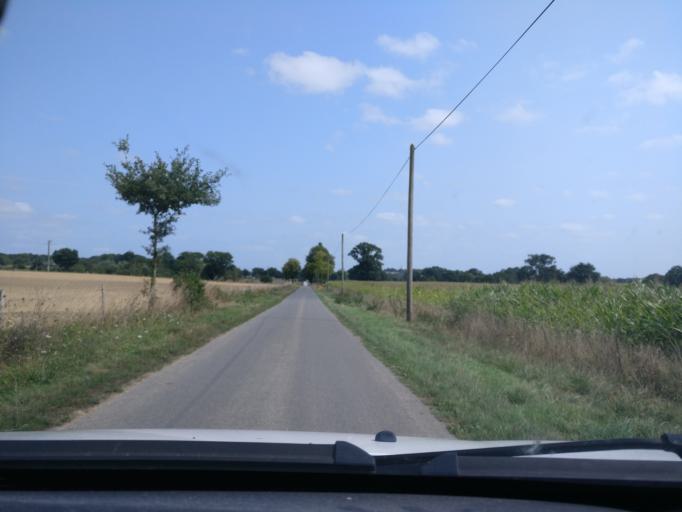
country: FR
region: Brittany
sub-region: Departement d'Ille-et-Vilaine
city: Erce-pres-Liffre
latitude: 48.2593
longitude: -1.5055
